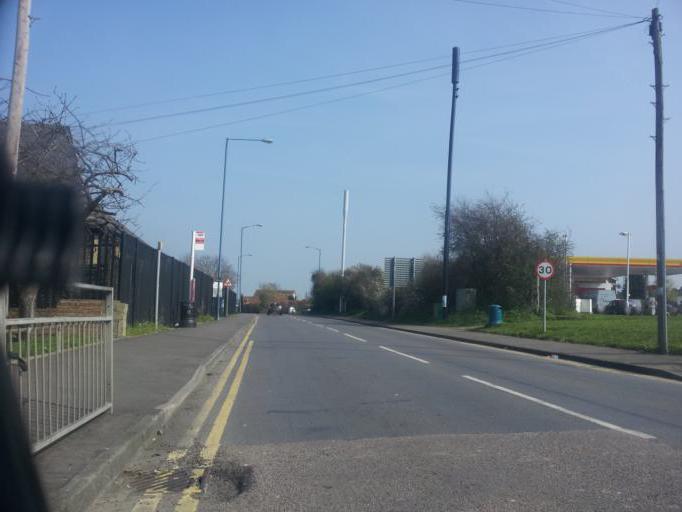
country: GB
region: England
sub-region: Kent
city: Gravesend
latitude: 51.4324
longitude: 0.3944
